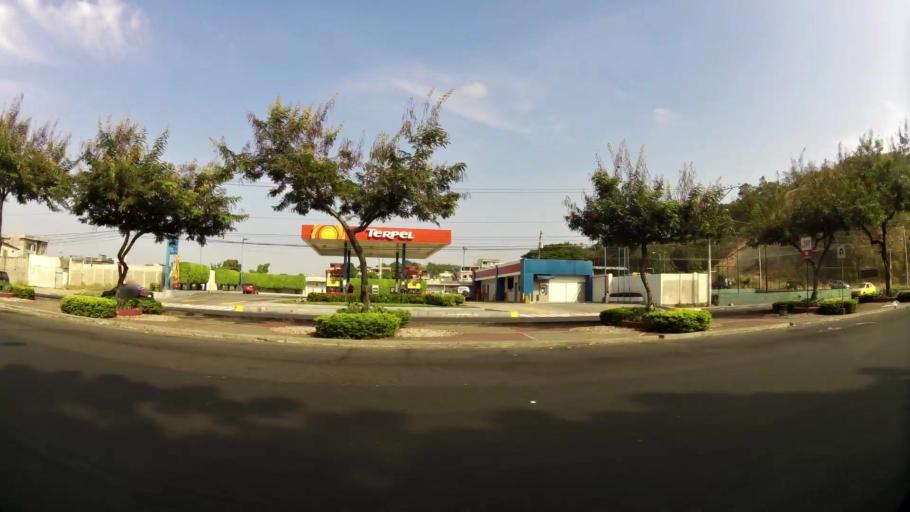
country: EC
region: Guayas
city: Guayaquil
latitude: -2.1872
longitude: -79.9122
